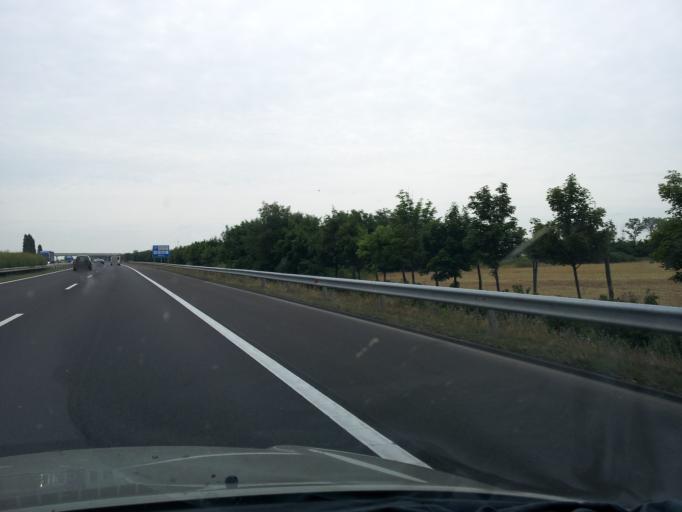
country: HU
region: Heves
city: Karacsond
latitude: 47.7040
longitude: 20.0565
